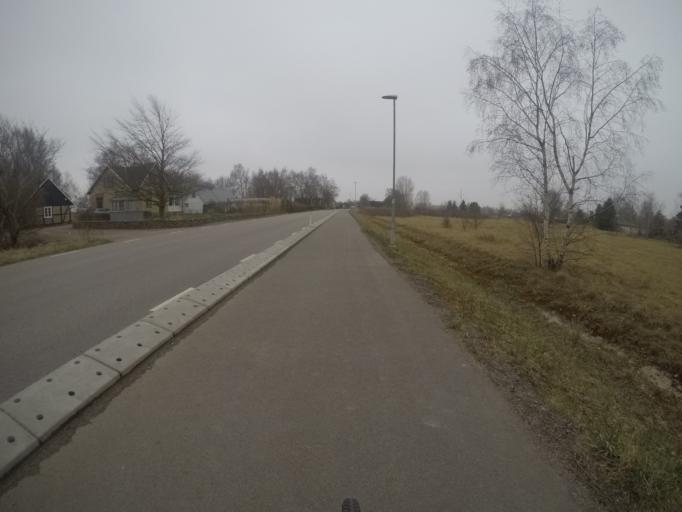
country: SE
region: Skane
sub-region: Angelholms Kommun
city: Vejbystrand
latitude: 56.2224
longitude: 12.7238
